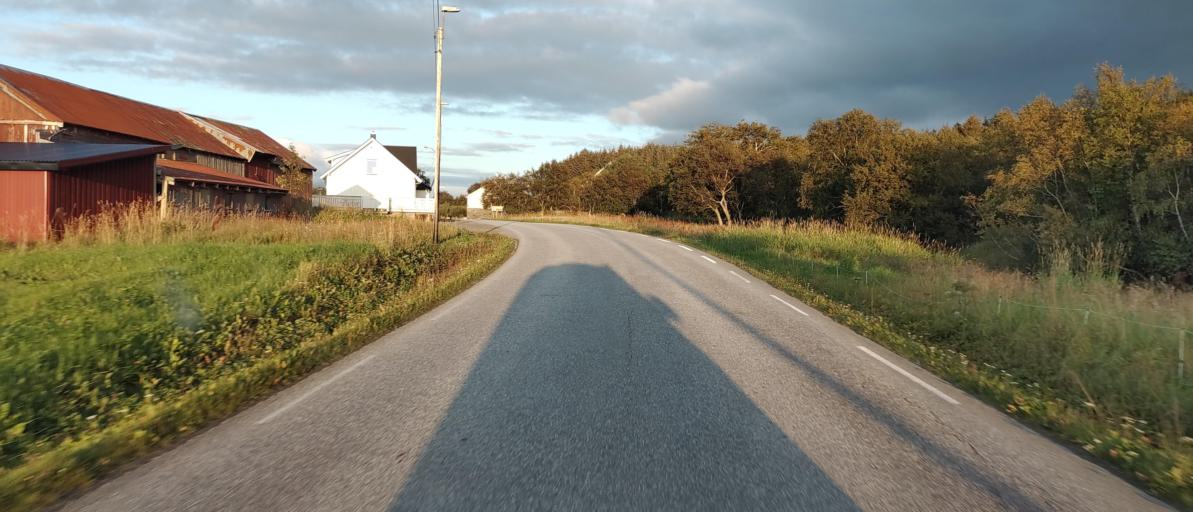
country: NO
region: More og Romsdal
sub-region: Fraena
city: Elnesvagen
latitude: 62.9889
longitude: 7.2052
